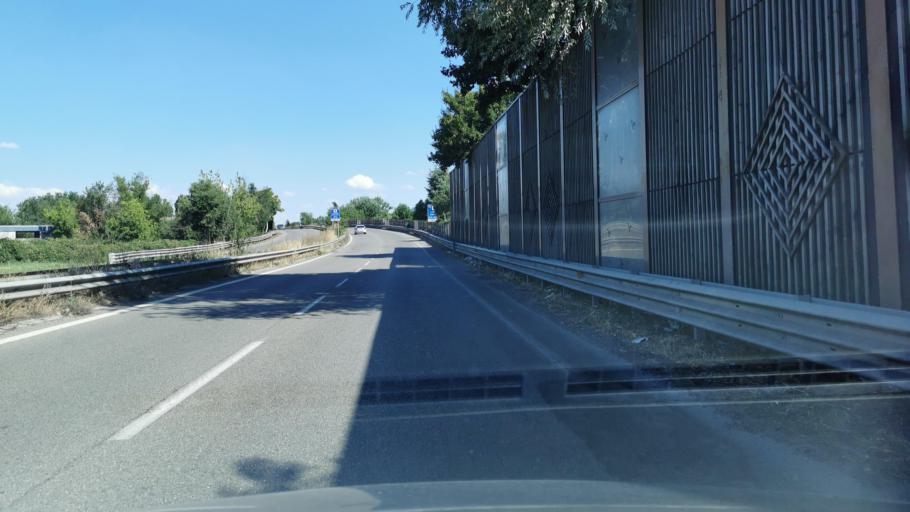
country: IT
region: Emilia-Romagna
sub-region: Provincia di Modena
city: Modena
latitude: 44.6613
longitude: 10.9434
